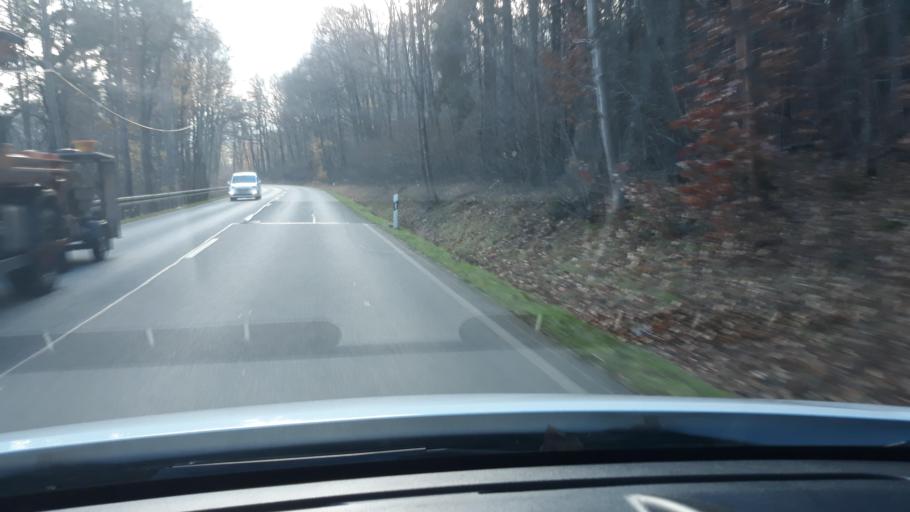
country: DE
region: Saxony
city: Wilkau-Hasslau
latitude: 50.6583
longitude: 12.5229
